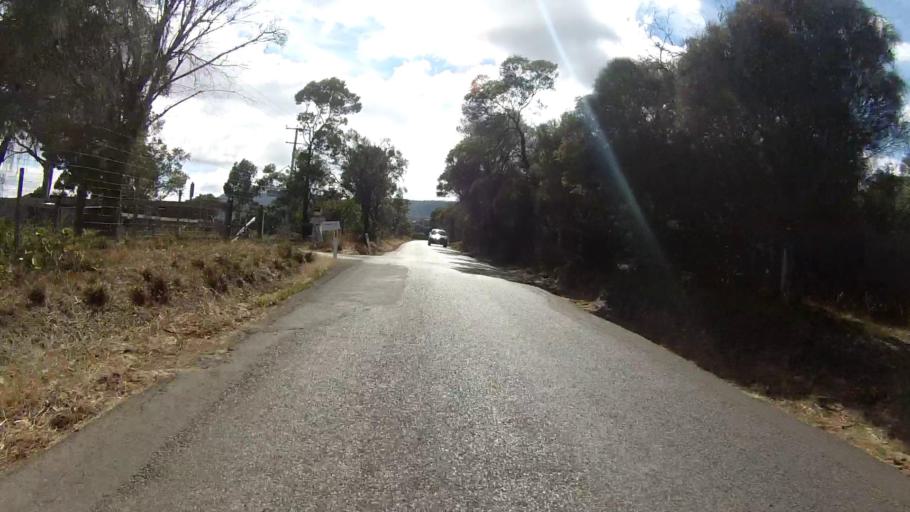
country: AU
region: Tasmania
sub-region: Brighton
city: Old Beach
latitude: -42.7720
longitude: 147.2893
